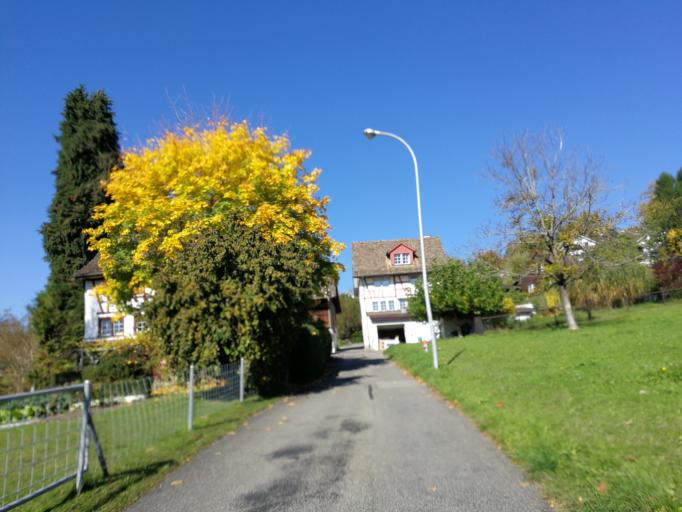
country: CH
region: Zurich
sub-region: Bezirk Meilen
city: Stafa
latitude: 47.2503
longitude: 8.7222
